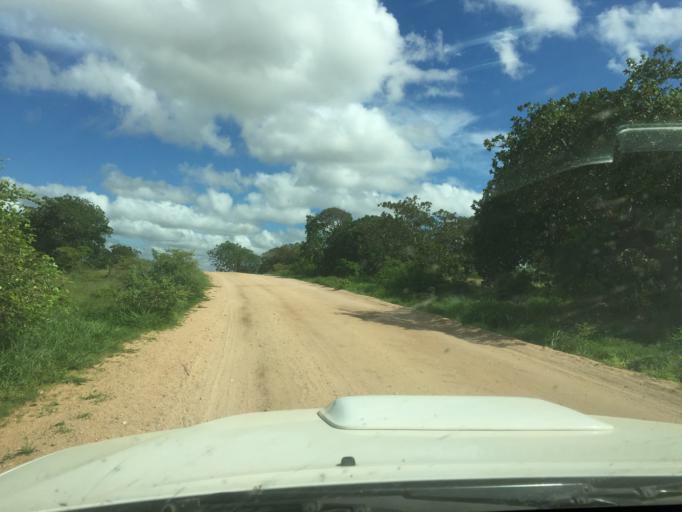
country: MZ
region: Nampula
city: Nacala
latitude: -14.2344
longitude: 40.5092
